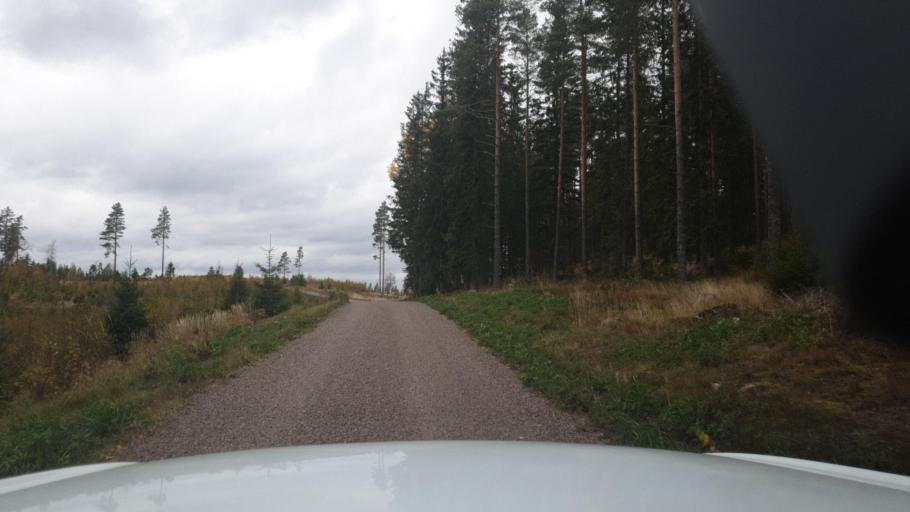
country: SE
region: Vaermland
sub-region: Torsby Kommun
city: Torsby
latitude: 59.9532
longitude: 12.7782
